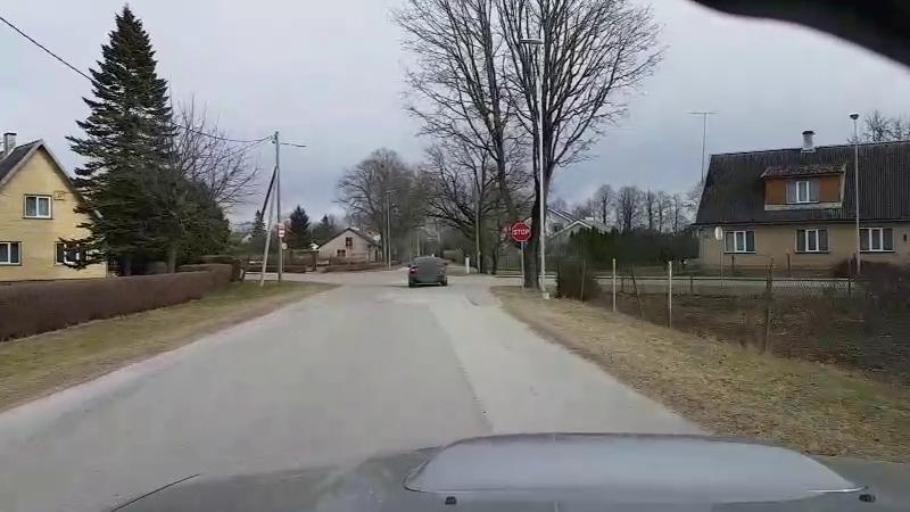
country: EE
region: Jaervamaa
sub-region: Paide linn
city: Paide
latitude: 58.8863
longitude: 25.5458
